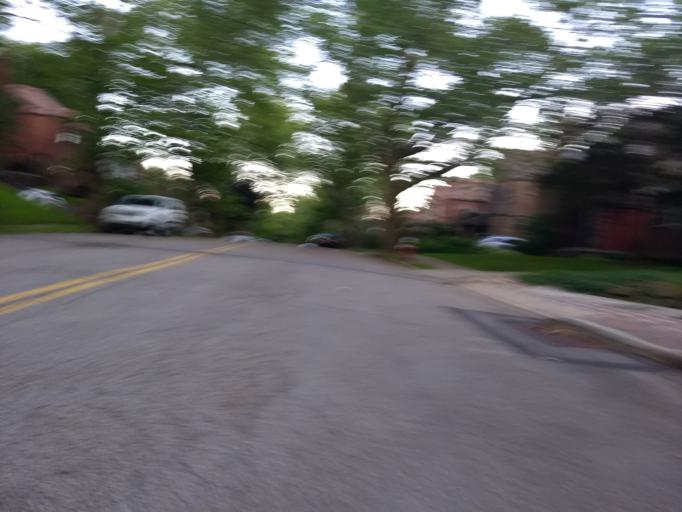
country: US
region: Pennsylvania
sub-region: Allegheny County
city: Homestead
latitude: 40.4302
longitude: -79.9330
